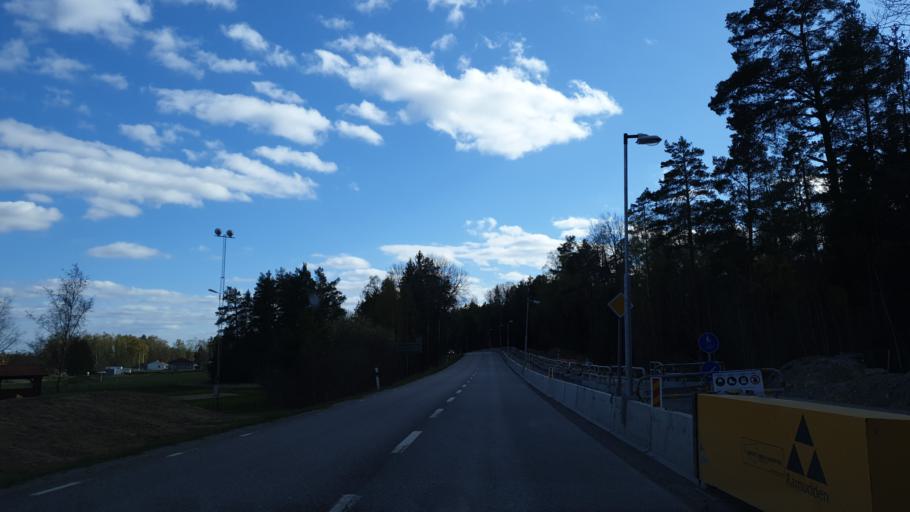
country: SE
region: Stockholm
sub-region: Sigtuna Kommun
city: Rosersberg
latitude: 59.6018
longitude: 17.8824
